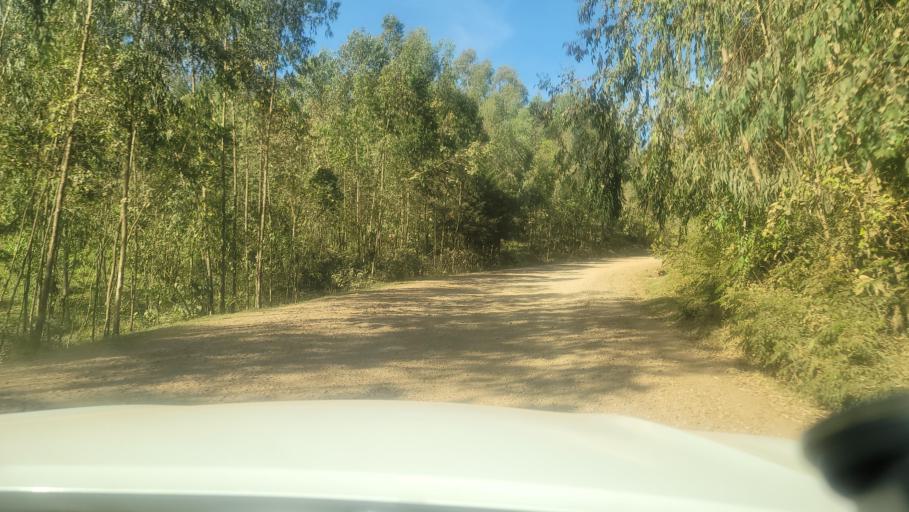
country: ET
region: Oromiya
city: Agaro
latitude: 7.8003
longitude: 36.4675
